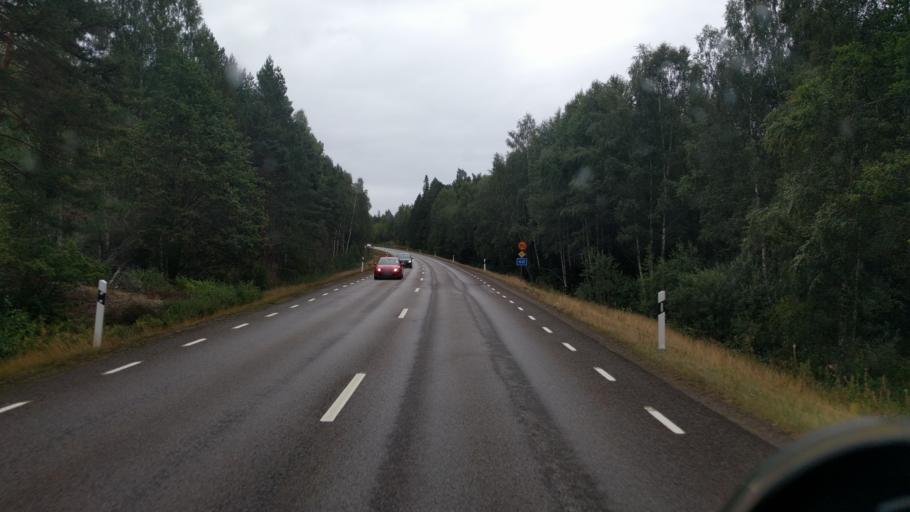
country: SE
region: Kalmar
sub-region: Vasterviks Kommun
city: Ankarsrum
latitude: 57.7013
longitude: 16.1642
